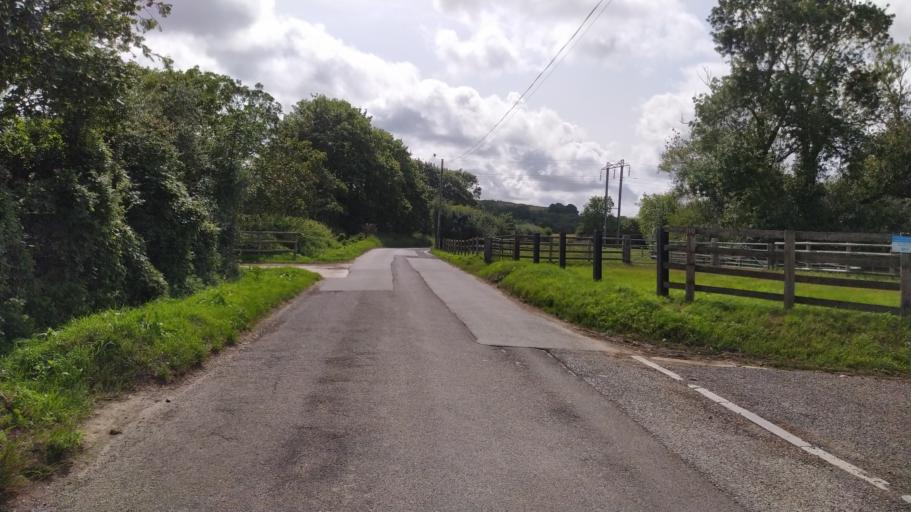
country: GB
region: England
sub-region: Dorset
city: Blandford Forum
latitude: 50.8228
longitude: -2.1121
